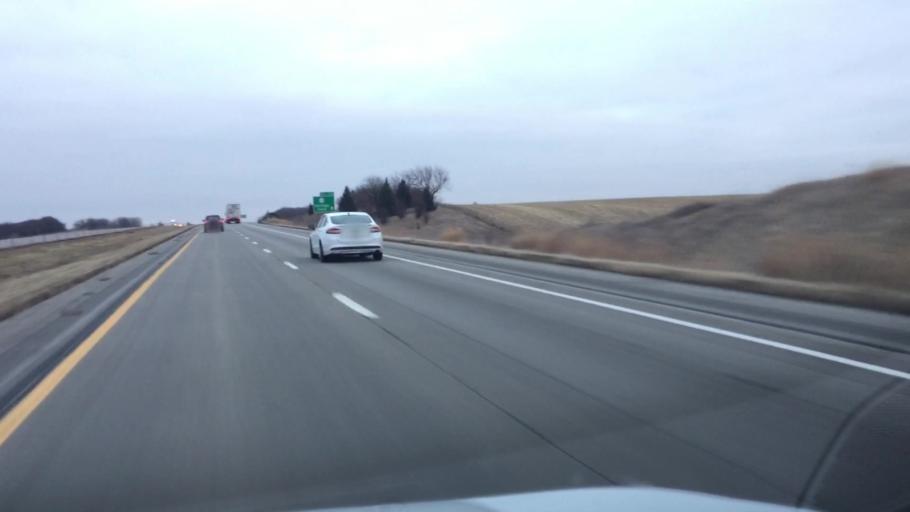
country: US
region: Iowa
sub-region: Jasper County
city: Newton
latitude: 41.6816
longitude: -92.9130
